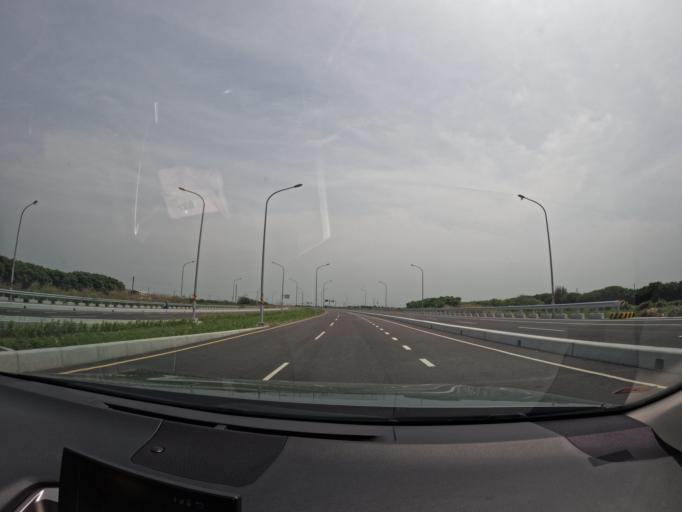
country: TW
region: Taiwan
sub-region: Changhua
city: Chang-hua
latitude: 23.9367
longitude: 120.3291
